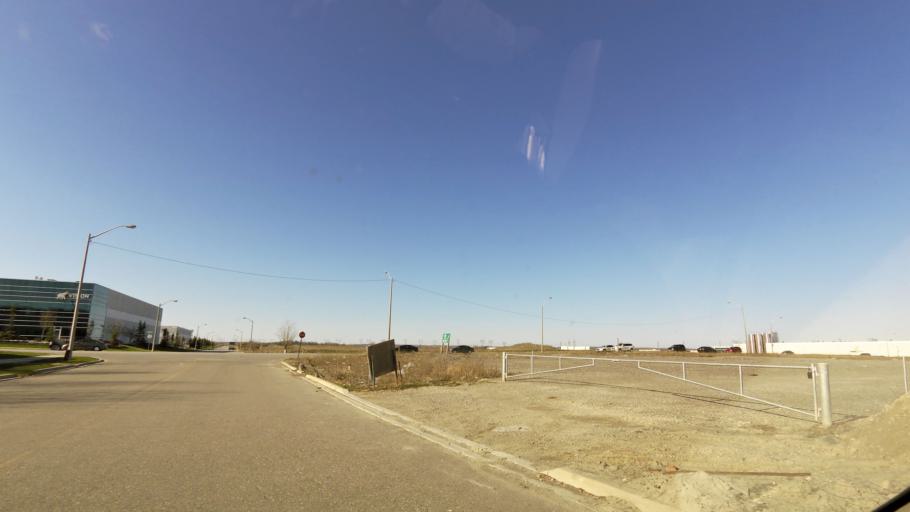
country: CA
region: Ontario
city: Etobicoke
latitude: 43.7750
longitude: -79.6388
